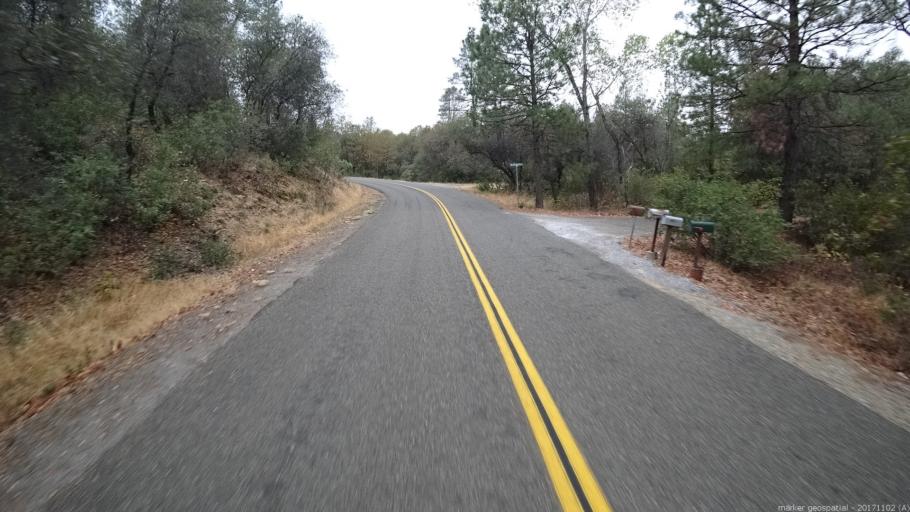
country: US
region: California
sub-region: Shasta County
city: Central Valley (historical)
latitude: 40.6611
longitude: -122.4158
